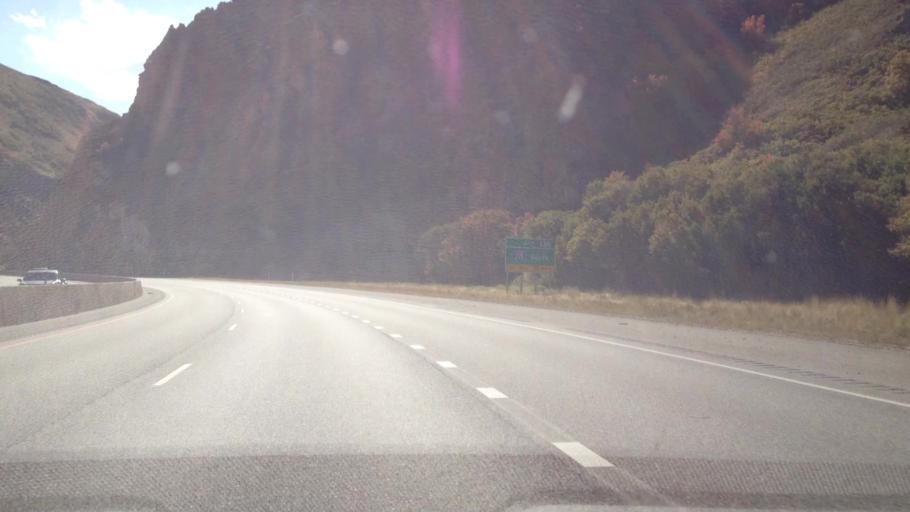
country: US
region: Utah
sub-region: Salt Lake County
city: East Millcreek
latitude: 40.7187
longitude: -111.7829
